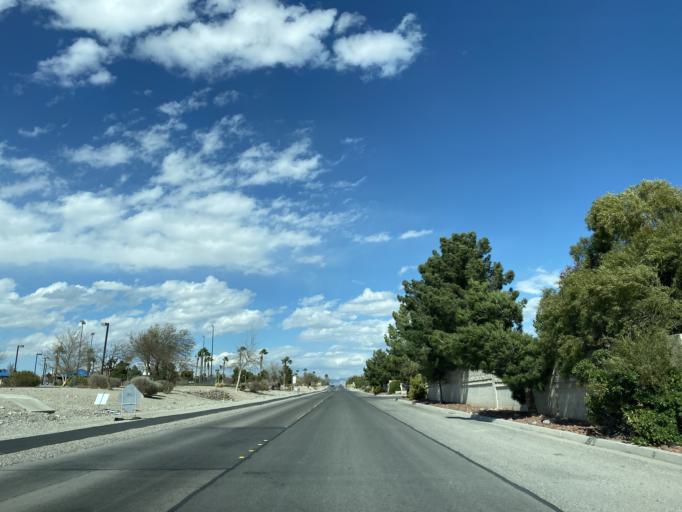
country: US
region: Nevada
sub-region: Clark County
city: Summerlin South
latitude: 36.2390
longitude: -115.3086
